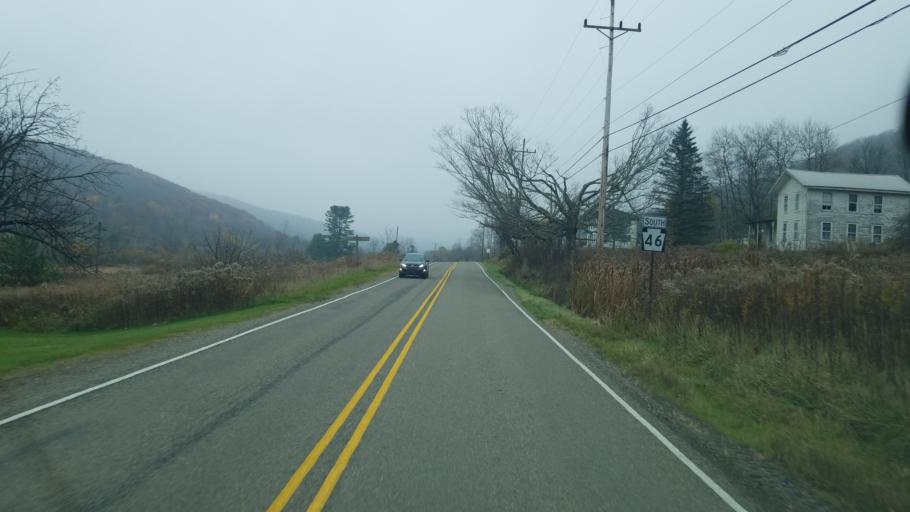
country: US
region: Pennsylvania
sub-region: McKean County
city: Smethport
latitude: 41.8823
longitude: -78.4930
